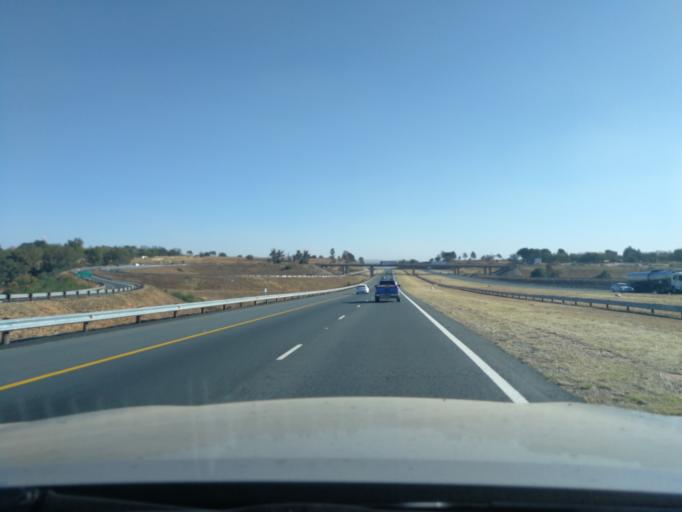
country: ZA
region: Gauteng
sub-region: West Rand District Municipality
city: Muldersdriseloop
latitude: -26.0187
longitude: 27.8642
